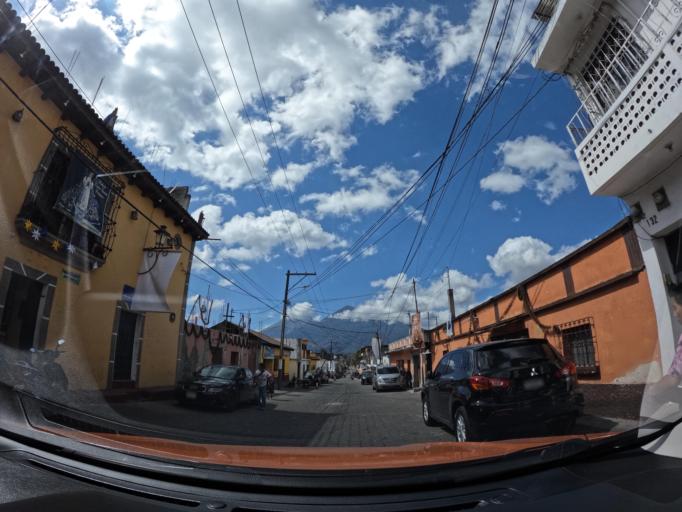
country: GT
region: Sacatepequez
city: Ciudad Vieja
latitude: 14.5253
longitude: -90.7562
